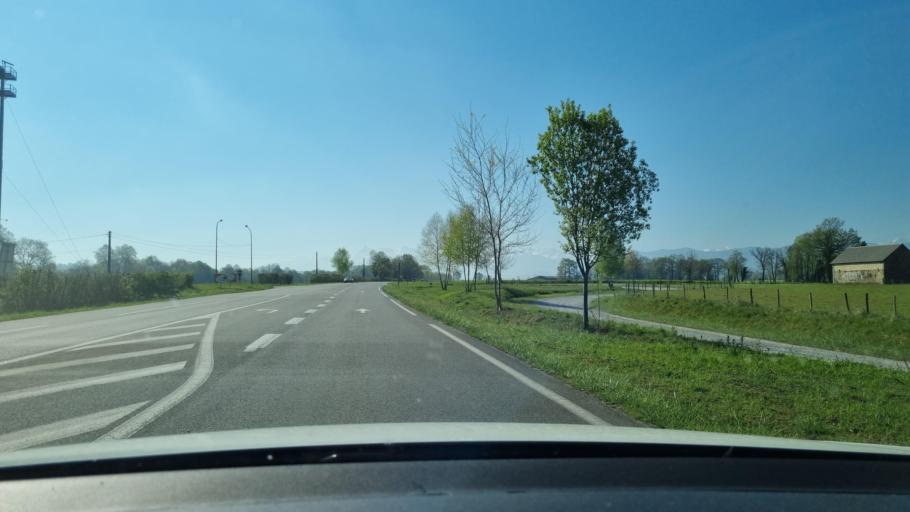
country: FR
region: Aquitaine
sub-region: Departement des Pyrenees-Atlantiques
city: Pontacq
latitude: 43.2106
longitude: -0.1375
